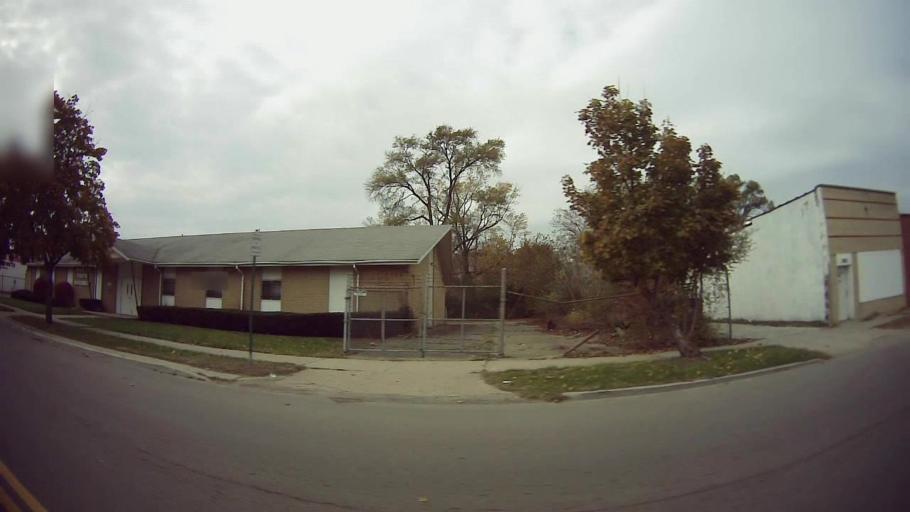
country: US
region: Michigan
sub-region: Oakland County
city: Hazel Park
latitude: 42.4434
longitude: -83.1027
